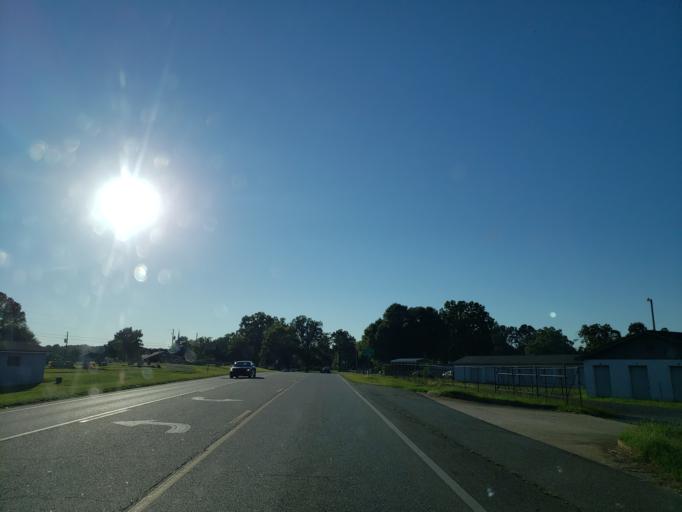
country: US
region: Georgia
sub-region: Polk County
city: Aragon
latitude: 34.0411
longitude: -85.0570
